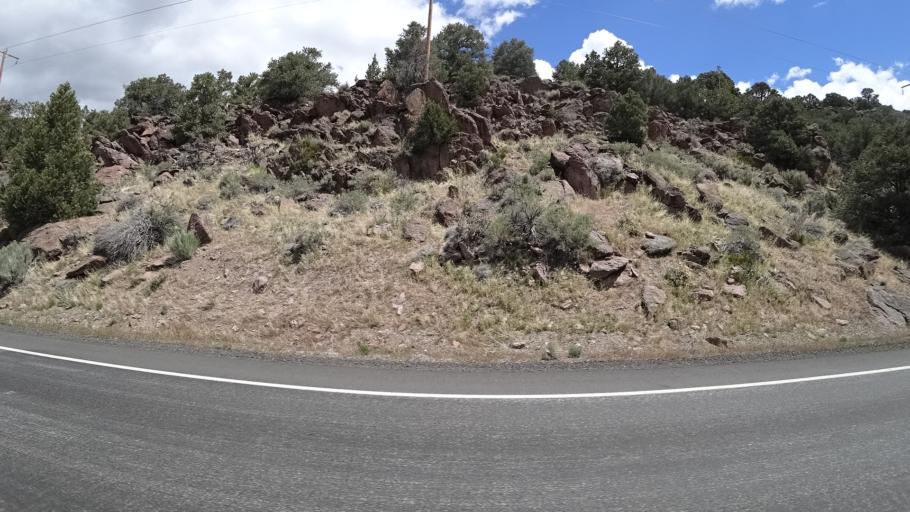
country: US
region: California
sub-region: Mono County
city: Bridgeport
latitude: 38.2015
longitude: -119.2227
